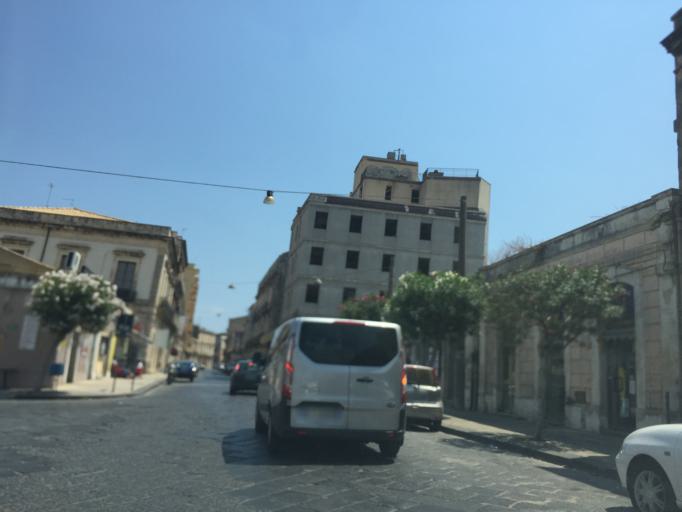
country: IT
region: Sicily
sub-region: Provincia di Siracusa
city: Siracusa
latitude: 37.0685
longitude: 15.2806
